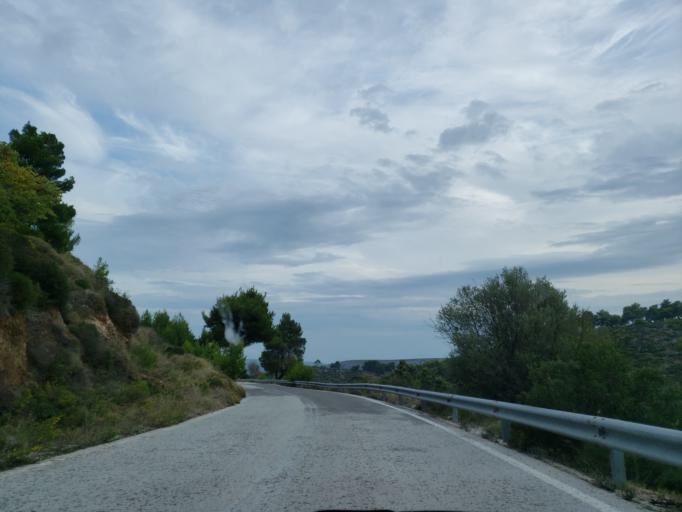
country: GR
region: Attica
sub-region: Nomarchia Anatolikis Attikis
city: Varnavas
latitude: 38.2121
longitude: 23.9431
